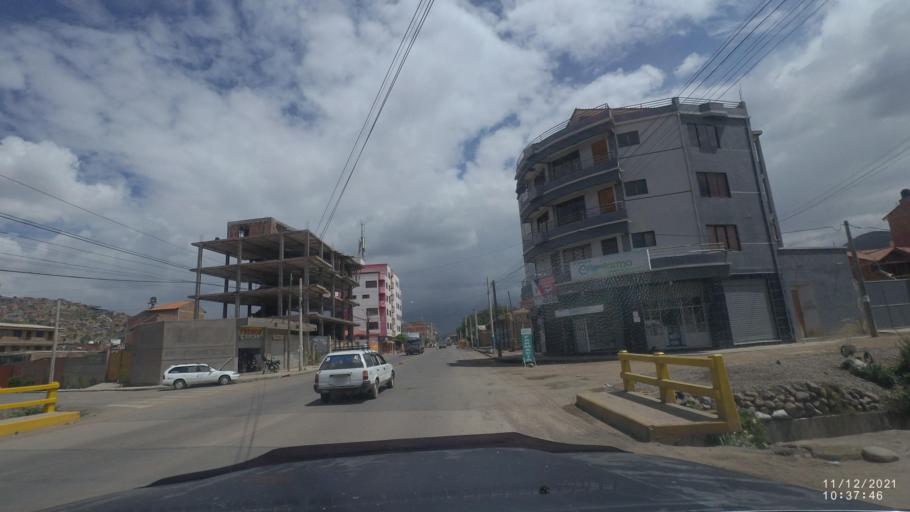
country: BO
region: Cochabamba
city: Cochabamba
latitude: -17.4434
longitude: -66.1251
